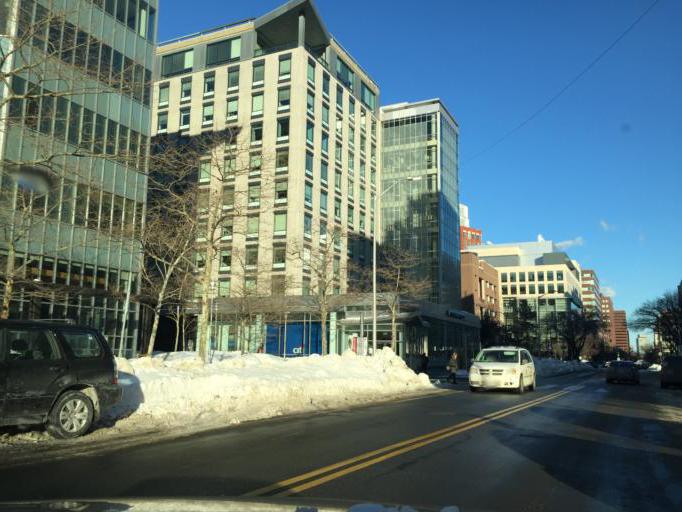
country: US
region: Massachusetts
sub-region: Middlesex County
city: Cambridge
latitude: 42.3628
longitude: -71.0919
